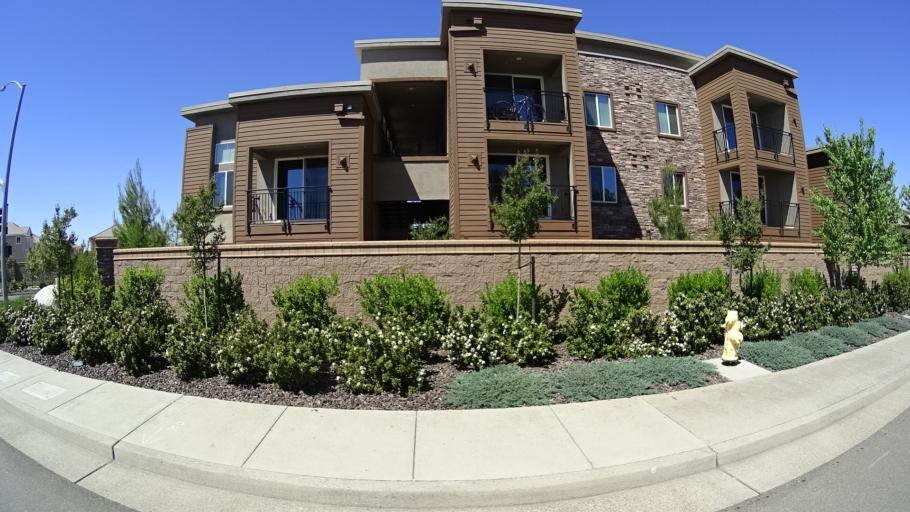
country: US
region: California
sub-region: Placer County
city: Loomis
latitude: 38.8026
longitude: -121.2103
